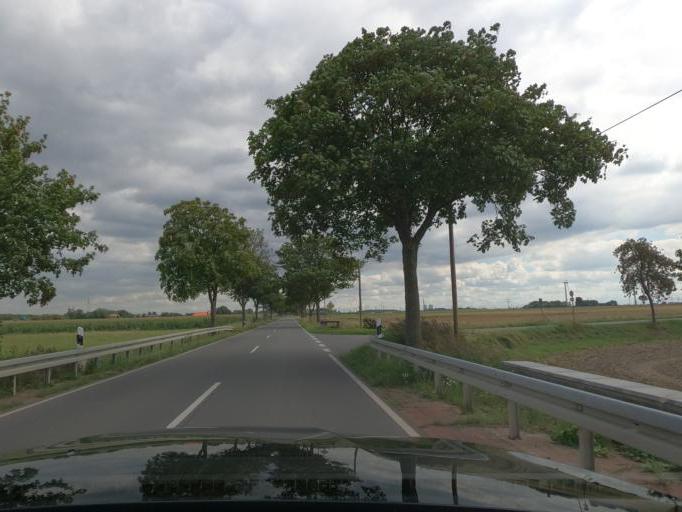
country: DE
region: Lower Saxony
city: Lehrte
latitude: 52.3630
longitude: 10.0002
